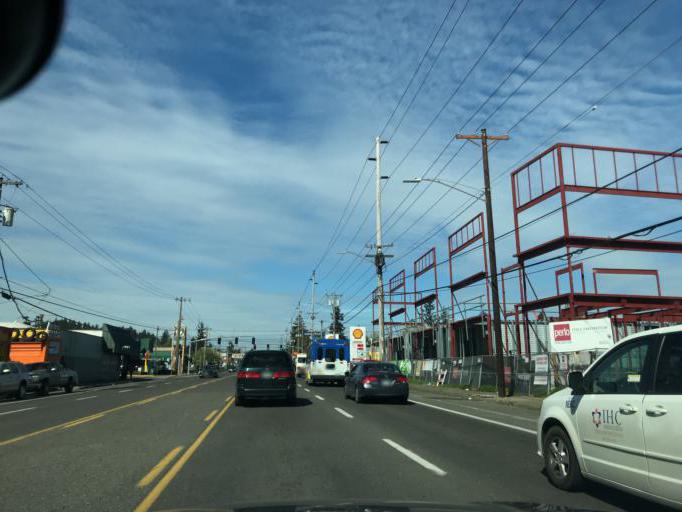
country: US
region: Oregon
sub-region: Multnomah County
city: Lents
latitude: 45.5041
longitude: -122.5359
